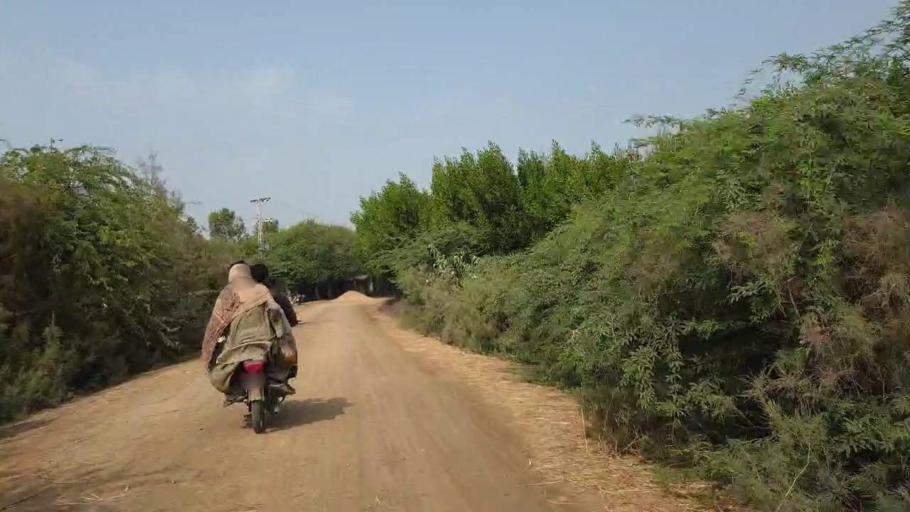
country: PK
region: Sindh
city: Kario
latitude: 24.7538
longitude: 68.5599
